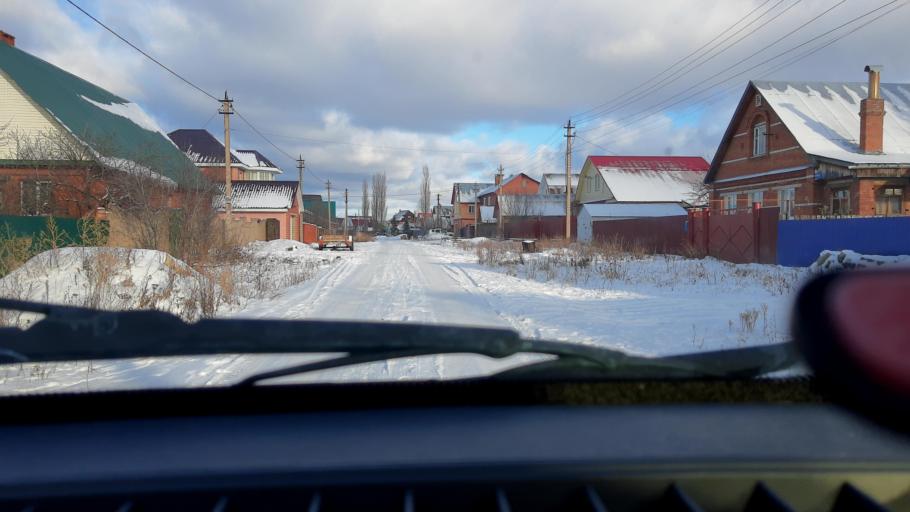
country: RU
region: Bashkortostan
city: Iglino
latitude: 54.7906
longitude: 56.2446
